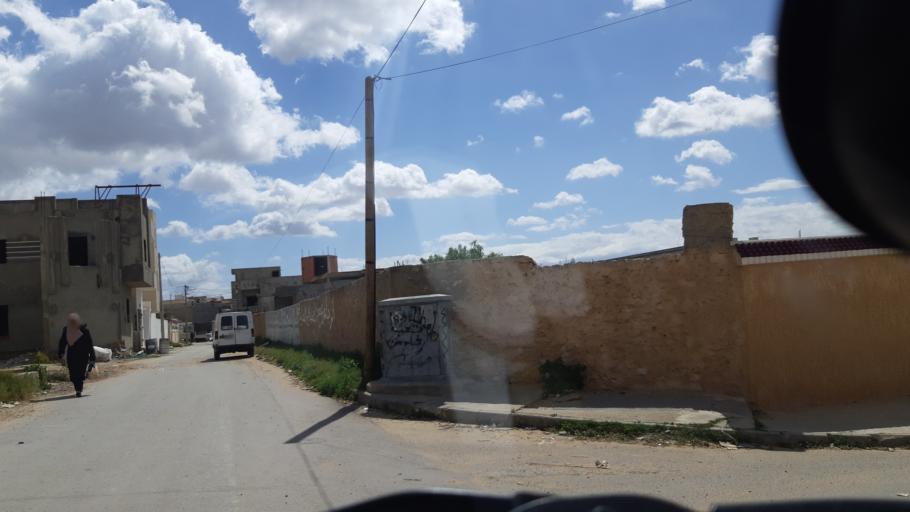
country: TN
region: Susah
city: Akouda
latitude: 35.8788
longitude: 10.5418
